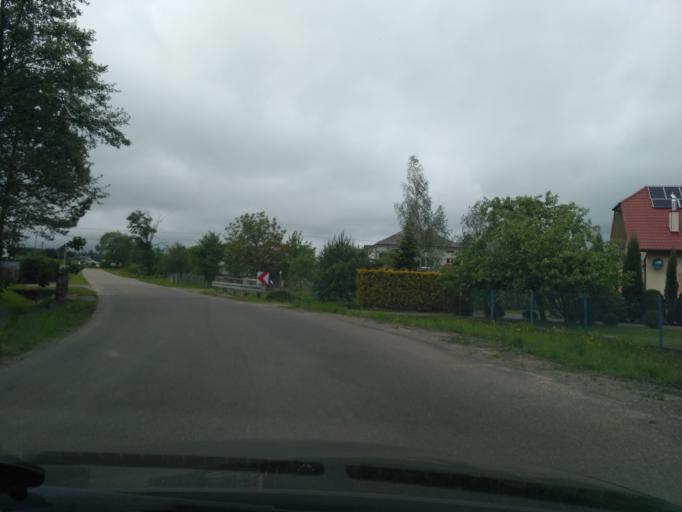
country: PL
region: Subcarpathian Voivodeship
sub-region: Powiat jasielski
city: Brzyska
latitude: 49.8214
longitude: 21.3961
